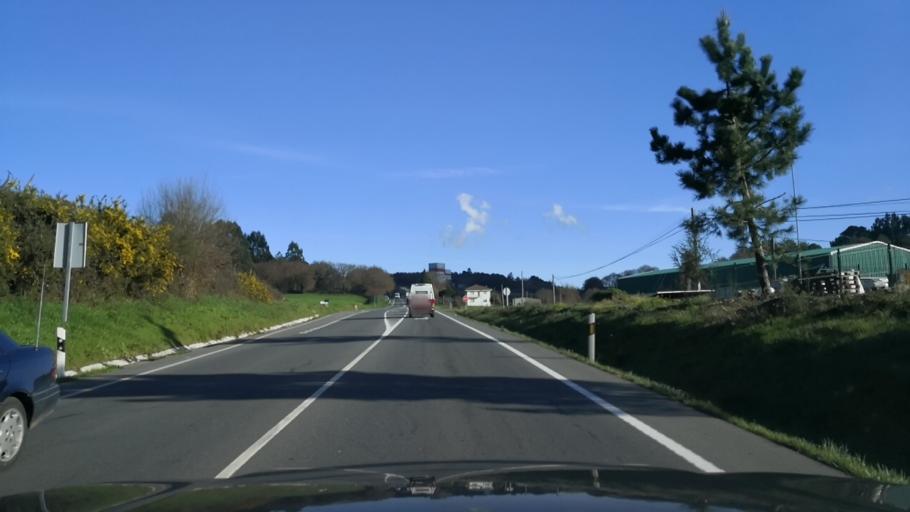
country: ES
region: Galicia
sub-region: Provincia de Pontevedra
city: Silleda
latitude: 42.7095
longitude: -8.2718
